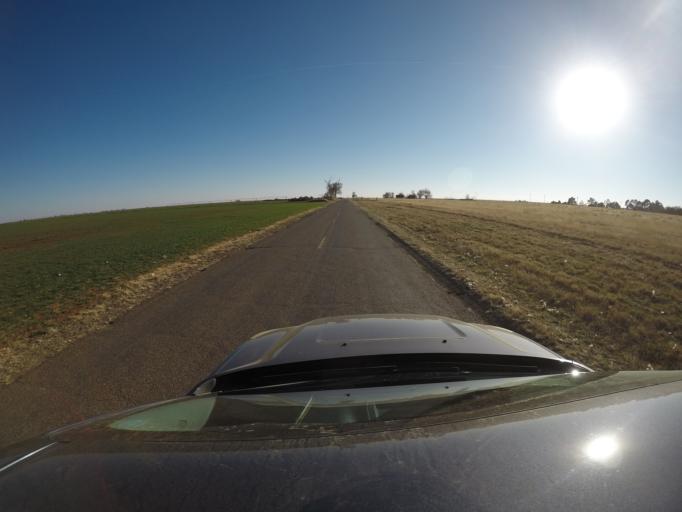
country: US
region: Texas
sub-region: Parmer County
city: Farwell
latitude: 34.3198
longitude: -103.0438
